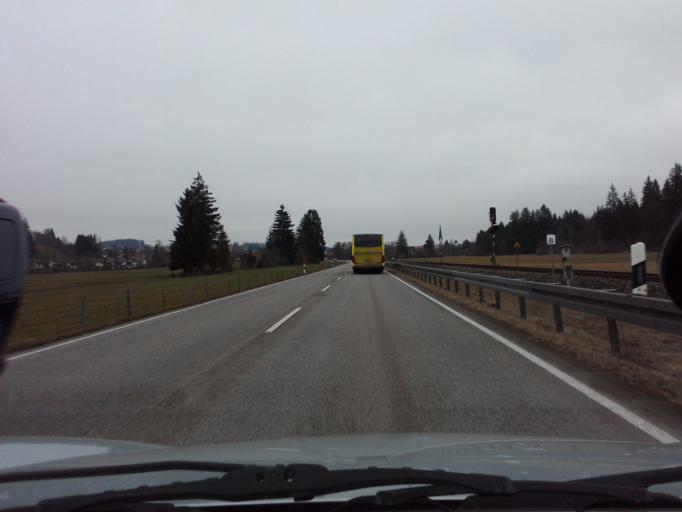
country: DE
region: Bavaria
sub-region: Swabia
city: Obermaiselstein
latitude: 47.4499
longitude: 10.2726
